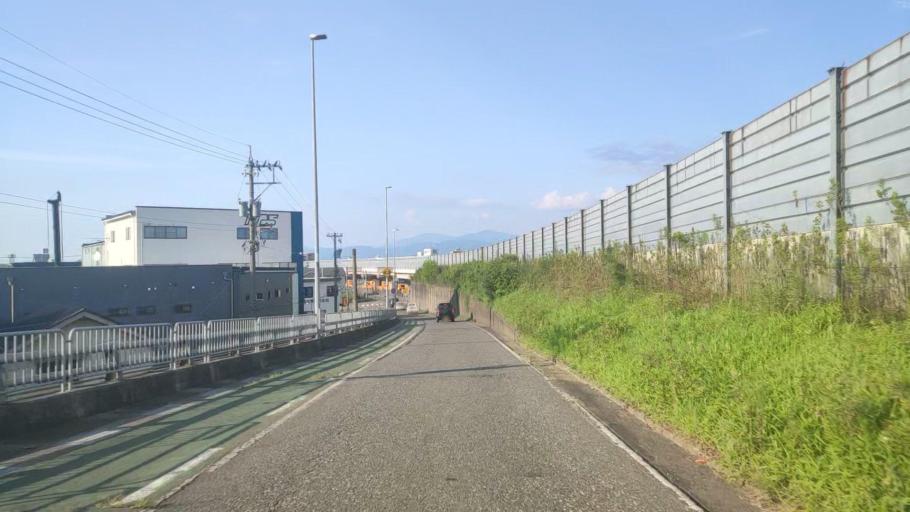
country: JP
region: Fukui
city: Fukui-shi
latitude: 36.0484
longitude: 136.2404
